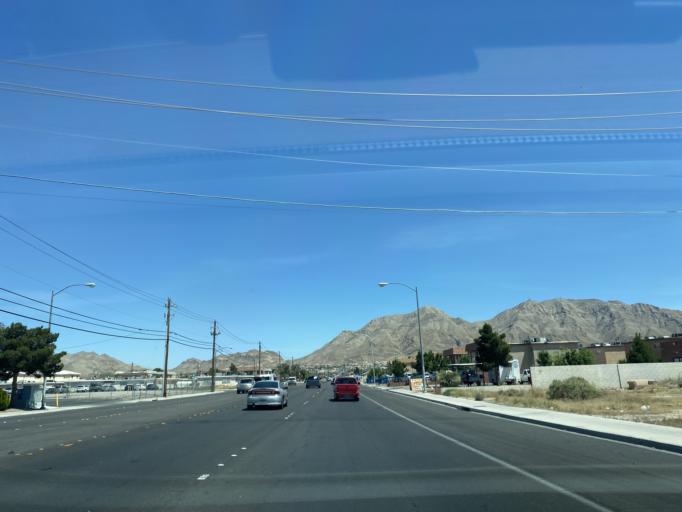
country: US
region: Nevada
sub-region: Clark County
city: Sunrise Manor
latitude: 36.1962
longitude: -115.0521
